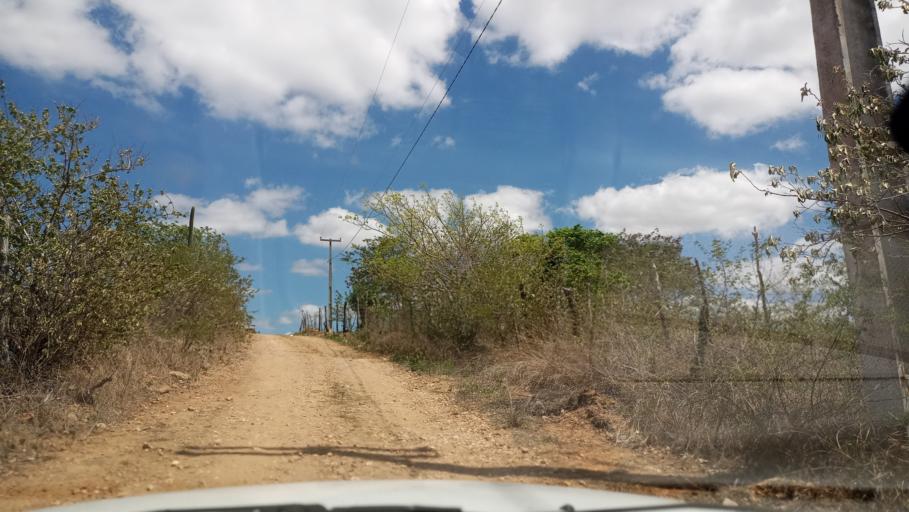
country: BR
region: Rio Grande do Norte
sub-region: Sao Paulo Do Potengi
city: Sao Paulo do Potengi
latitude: -5.7468
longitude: -35.9095
